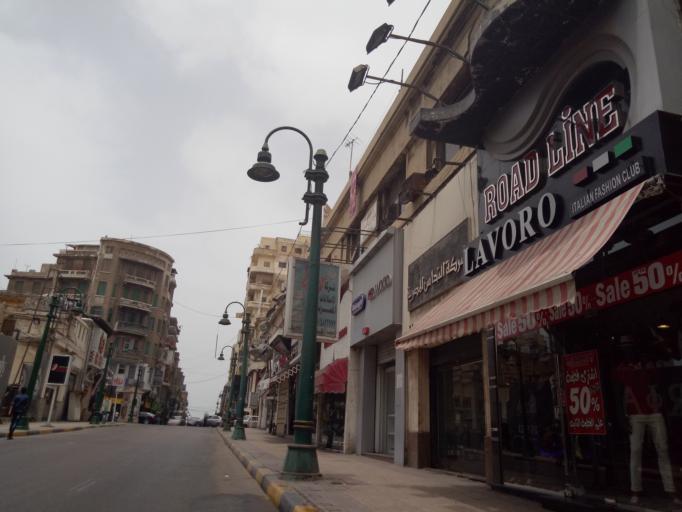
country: EG
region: Alexandria
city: Alexandria
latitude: 31.1984
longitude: 29.9033
